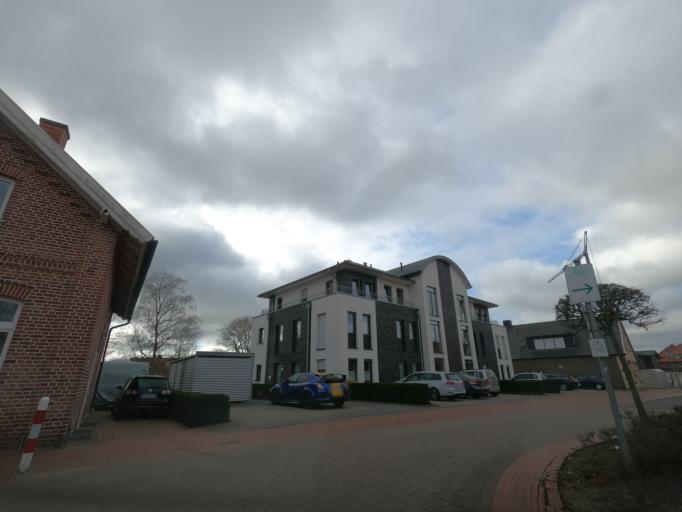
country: DE
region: Lower Saxony
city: Herzlake
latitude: 52.6848
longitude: 7.6016
